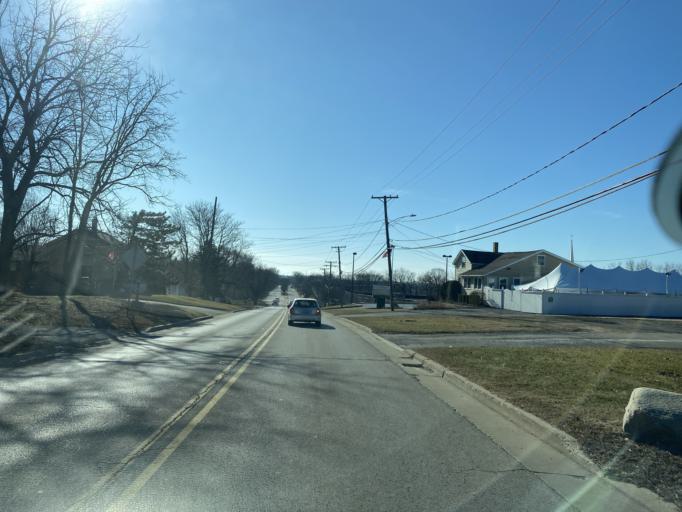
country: US
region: Illinois
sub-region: Will County
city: Lockport
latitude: 41.6037
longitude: -88.0507
